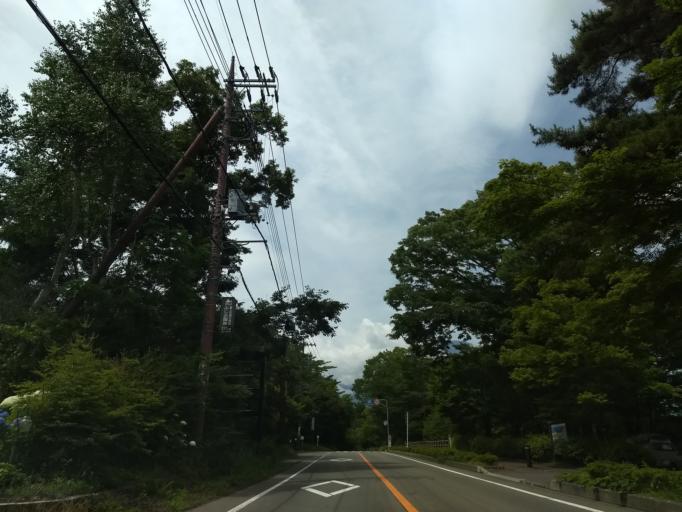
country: JP
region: Shizuoka
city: Gotemba
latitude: 35.4095
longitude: 138.8861
